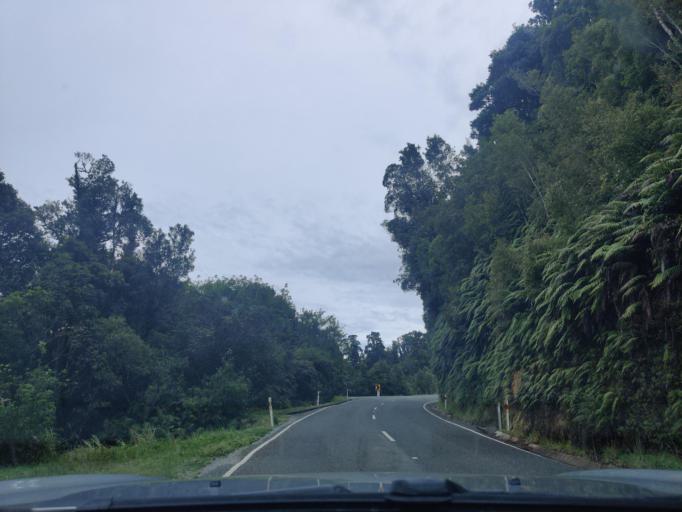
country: NZ
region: West Coast
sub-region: Westland District
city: Hokitika
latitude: -43.1766
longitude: 170.4558
